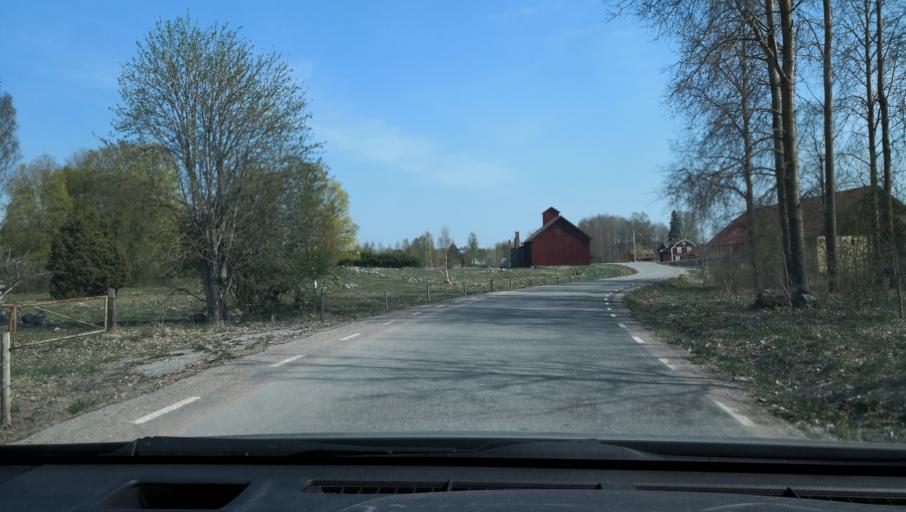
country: SE
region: Vaestmanland
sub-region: Sala Kommun
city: Sala
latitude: 60.0078
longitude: 16.6914
